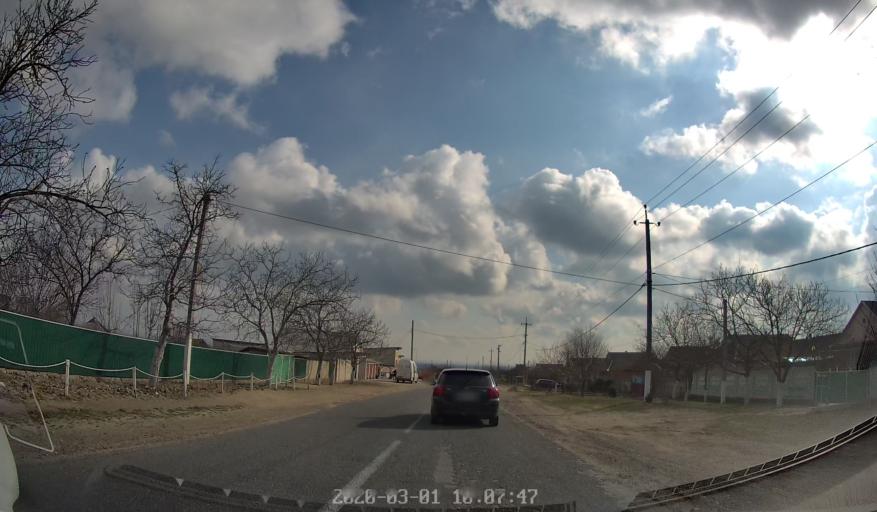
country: UA
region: Odessa
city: Starokozache
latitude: 46.4310
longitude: 30.0415
